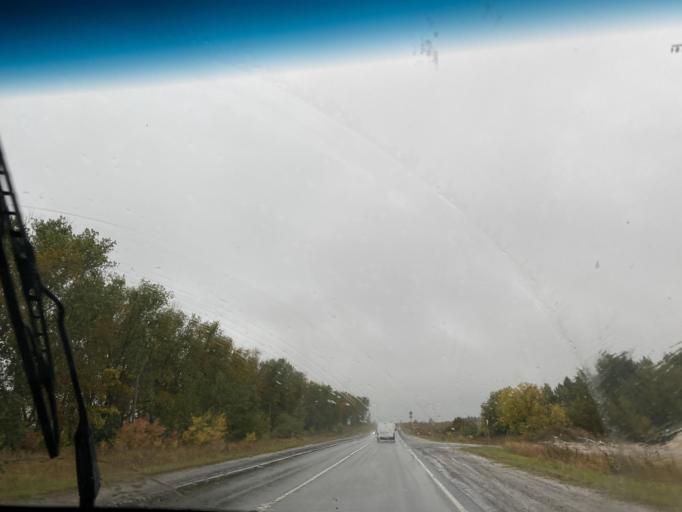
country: RU
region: Rjazan
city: Ryazan'
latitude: 54.4899
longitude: 39.8112
